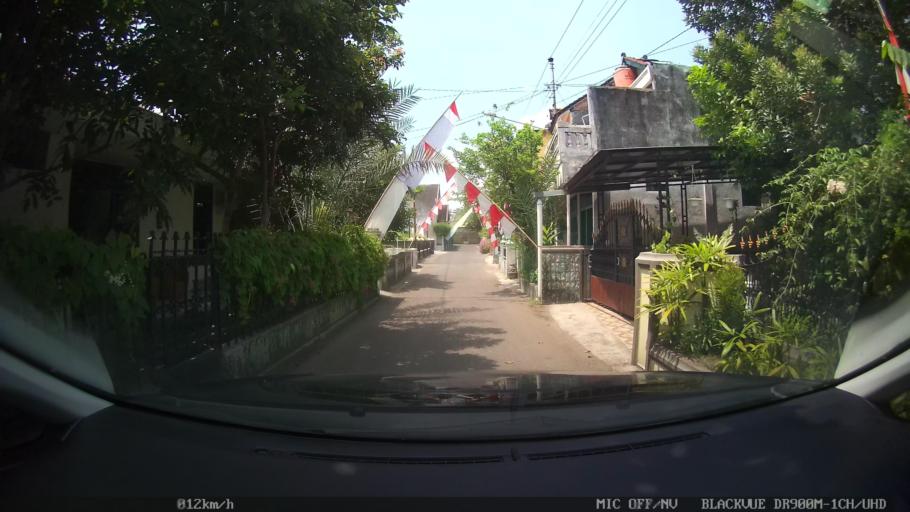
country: ID
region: Daerah Istimewa Yogyakarta
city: Yogyakarta
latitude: -7.8173
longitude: 110.3961
